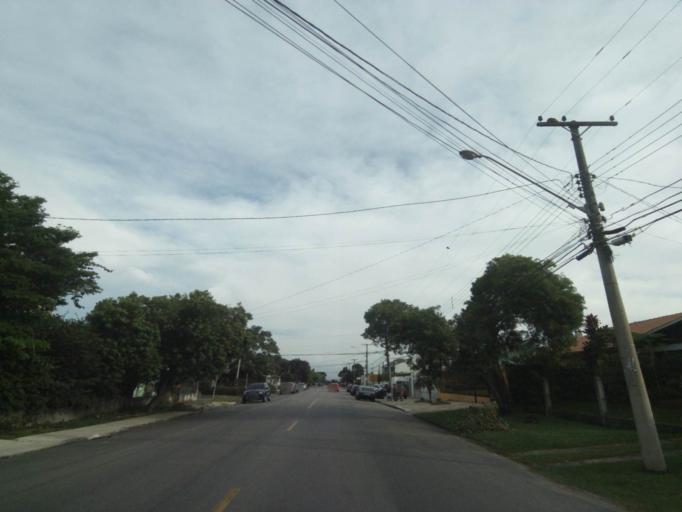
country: BR
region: Parana
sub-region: Pinhais
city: Pinhais
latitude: -25.4608
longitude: -49.2167
